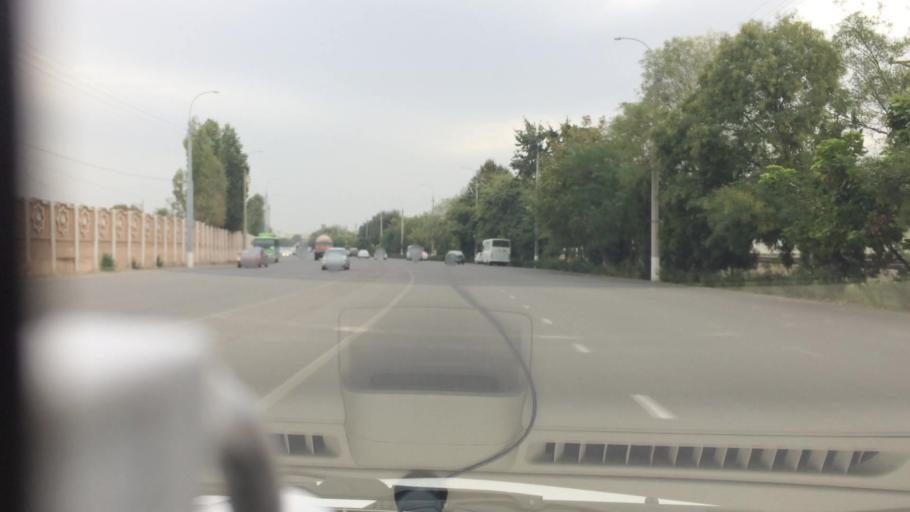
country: UZ
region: Toshkent
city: Salor
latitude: 41.3099
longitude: 69.3056
